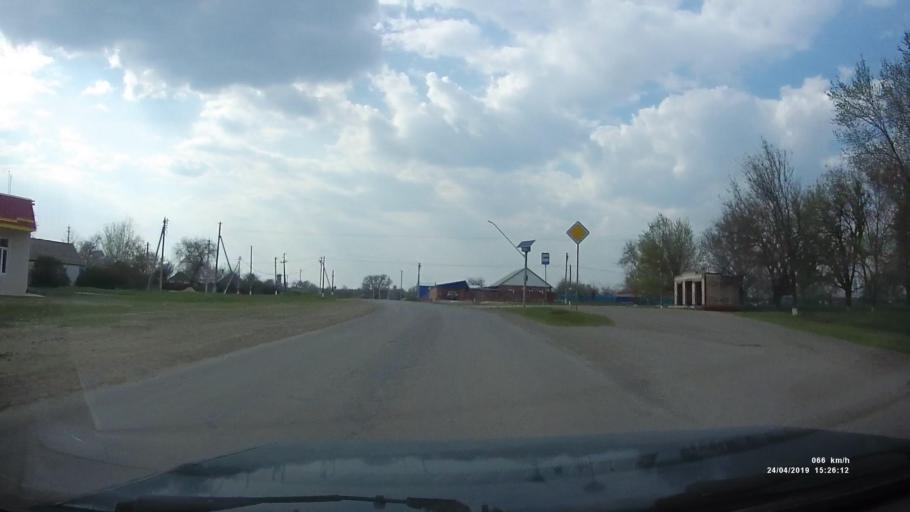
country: RU
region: Rostov
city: Remontnoye
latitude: 46.5570
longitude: 43.0360
